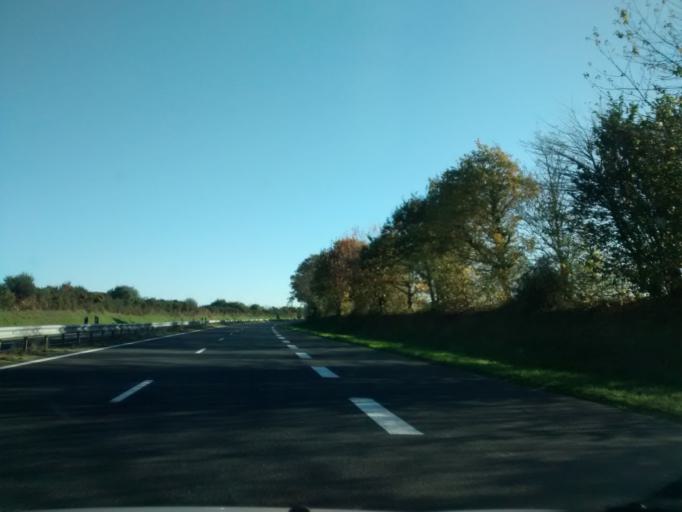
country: FR
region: Brittany
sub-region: Departement des Cotes-d'Armor
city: Cavan
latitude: 48.6811
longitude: -3.3574
